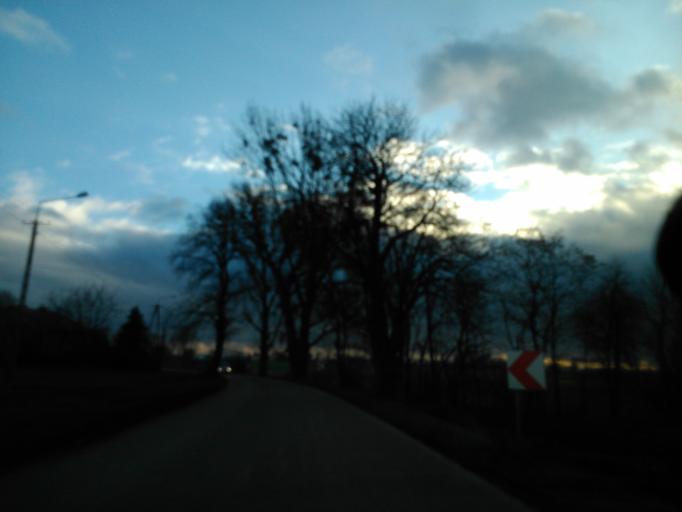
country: PL
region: Masovian Voivodeship
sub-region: Powiat warszawski zachodni
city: Blonie
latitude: 52.2138
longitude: 20.6526
